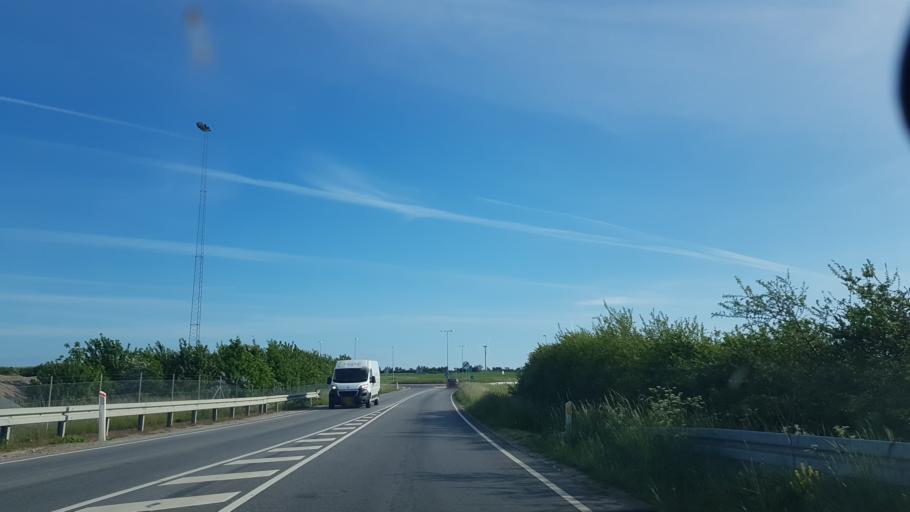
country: DK
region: Zealand
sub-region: Slagelse Kommune
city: Forlev
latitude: 55.3622
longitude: 11.2285
